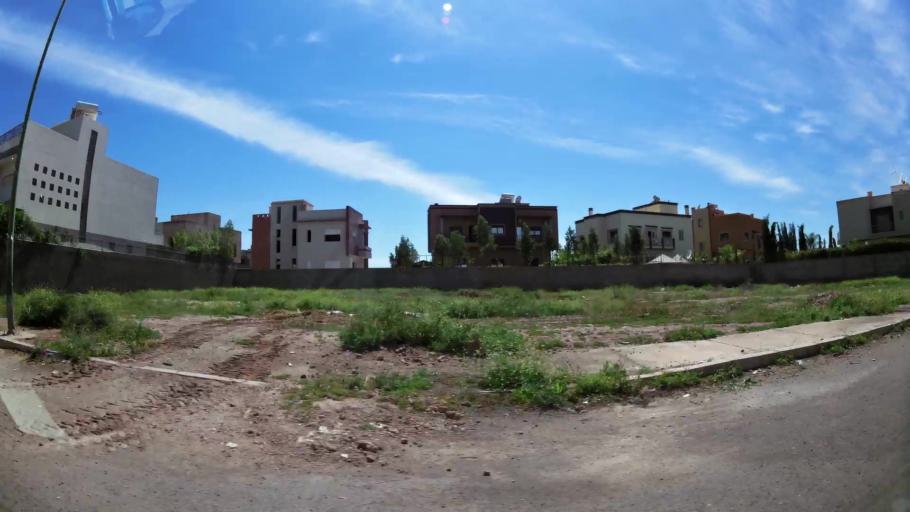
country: MA
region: Marrakech-Tensift-Al Haouz
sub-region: Marrakech
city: Marrakesh
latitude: 31.6538
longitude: -8.0734
